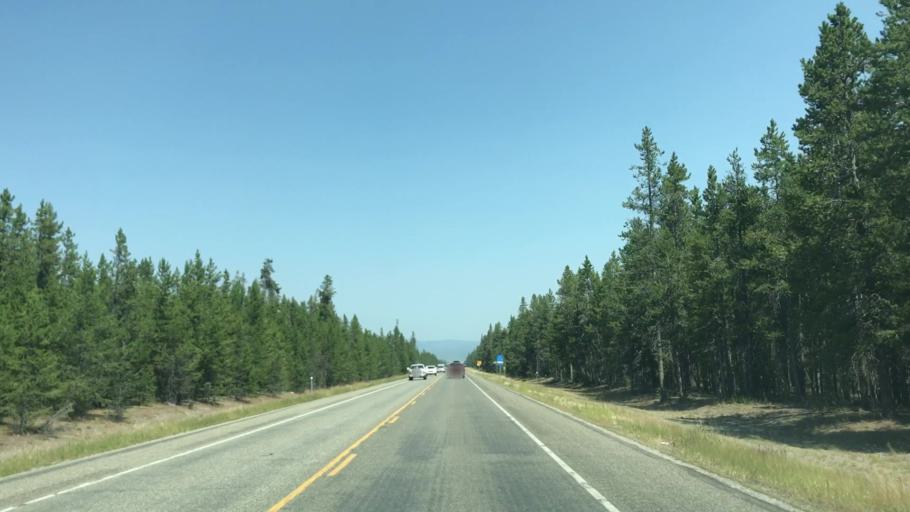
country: US
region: Montana
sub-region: Gallatin County
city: West Yellowstone
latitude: 44.6756
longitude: -111.1005
